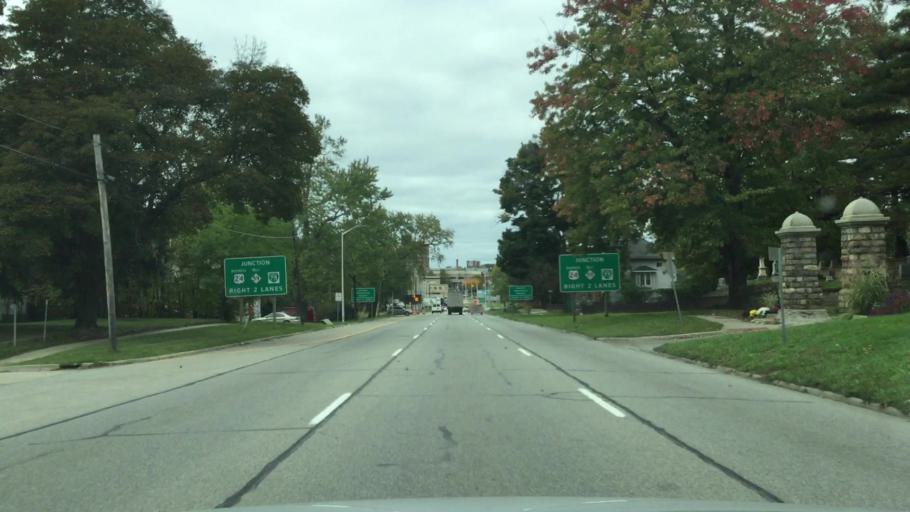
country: US
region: Michigan
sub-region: Oakland County
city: Pontiac
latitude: 42.6420
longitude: -83.2855
